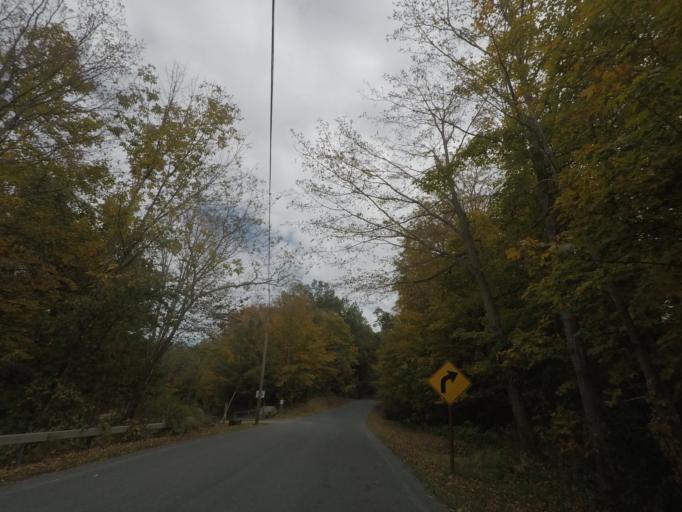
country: US
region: New York
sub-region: Rensselaer County
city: East Greenbush
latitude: 42.5554
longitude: -73.6578
